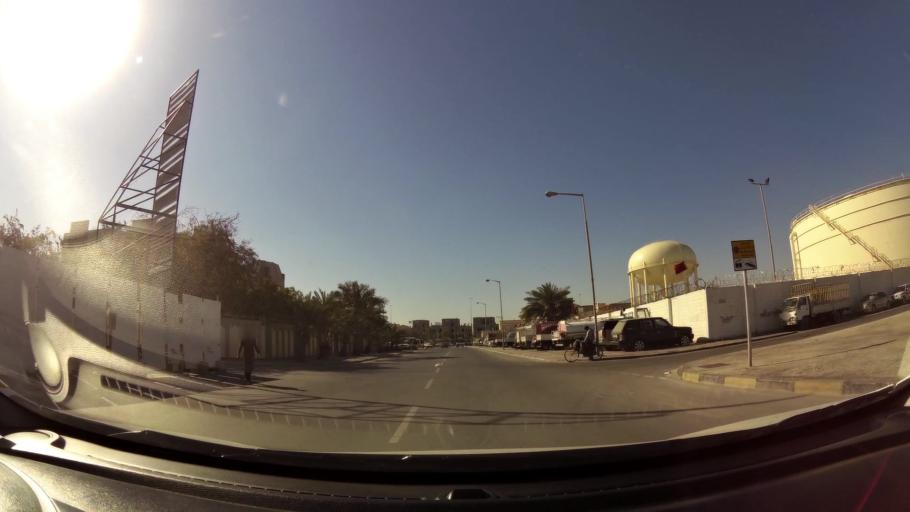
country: BH
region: Muharraq
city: Al Muharraq
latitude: 26.2547
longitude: 50.6058
